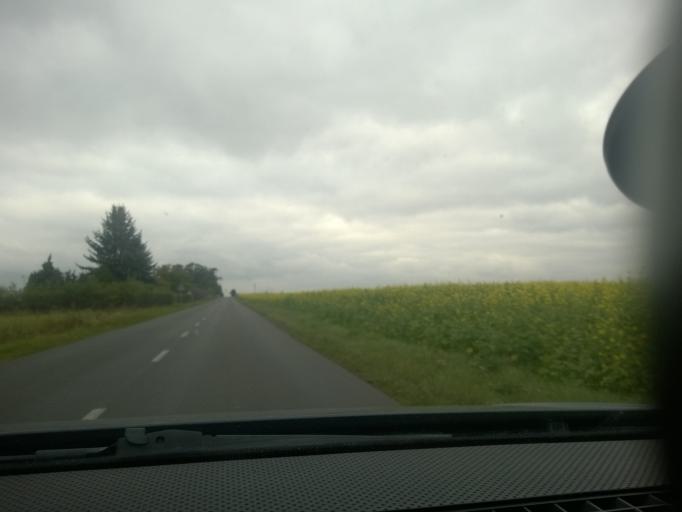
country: PL
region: Greater Poland Voivodeship
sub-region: Powiat kaliski
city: Opatowek
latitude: 51.7244
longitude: 18.1875
